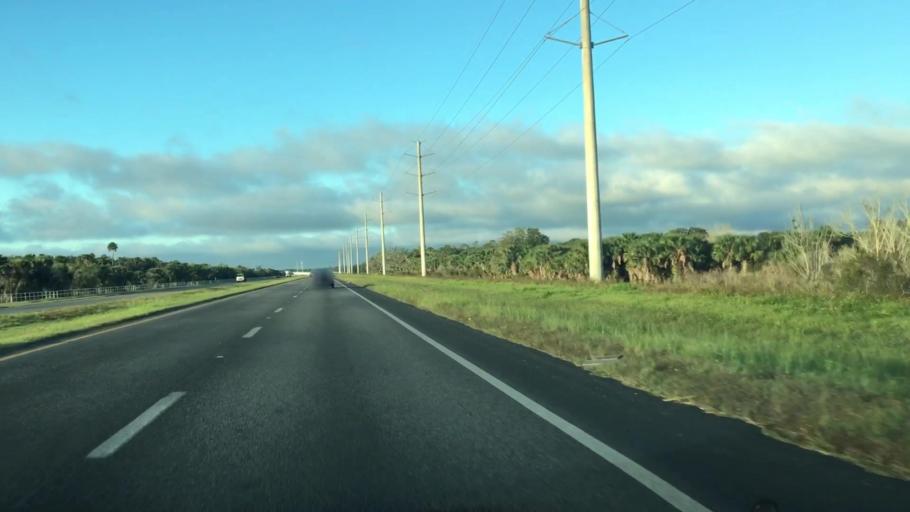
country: US
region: Florida
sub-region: Seminole County
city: Midway
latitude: 28.8153
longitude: -81.1917
